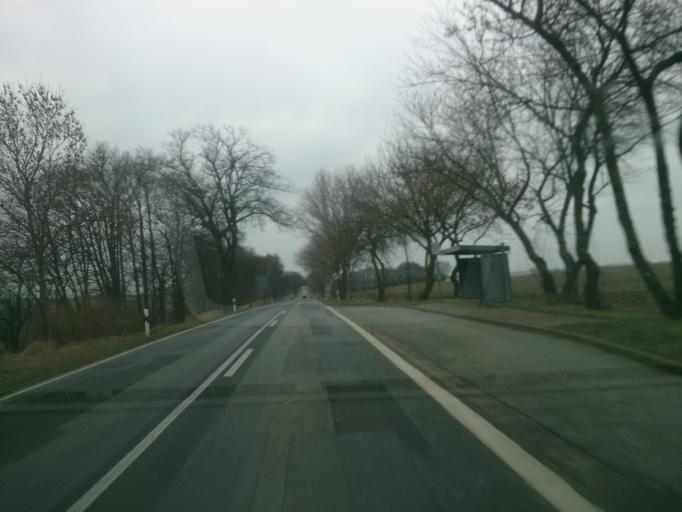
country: DE
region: Mecklenburg-Vorpommern
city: Borrentin
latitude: 53.7914
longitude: 12.9517
